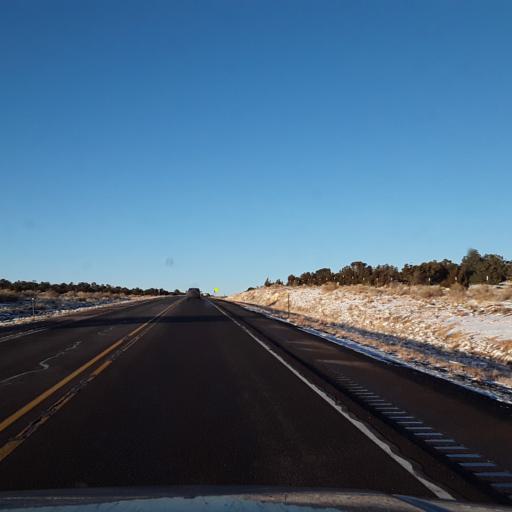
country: US
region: New Mexico
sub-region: Lincoln County
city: Carrizozo
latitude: 34.2157
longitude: -105.6476
